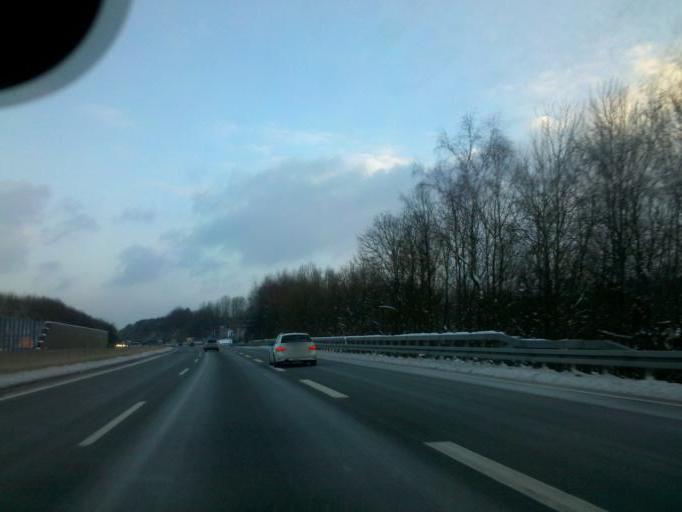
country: DE
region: North Rhine-Westphalia
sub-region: Regierungsbezirk Arnsberg
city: Wenden
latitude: 50.9365
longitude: 7.8807
